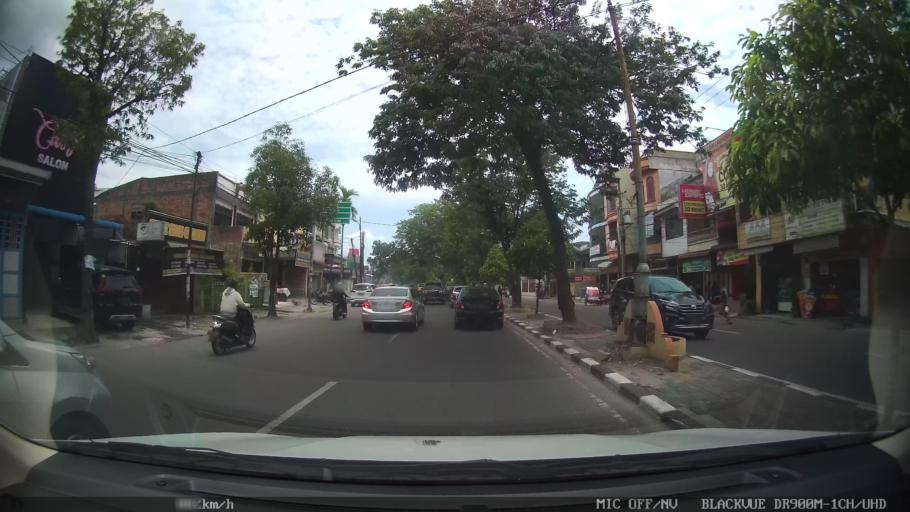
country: ID
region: North Sumatra
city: Medan
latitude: 3.5657
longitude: 98.6619
